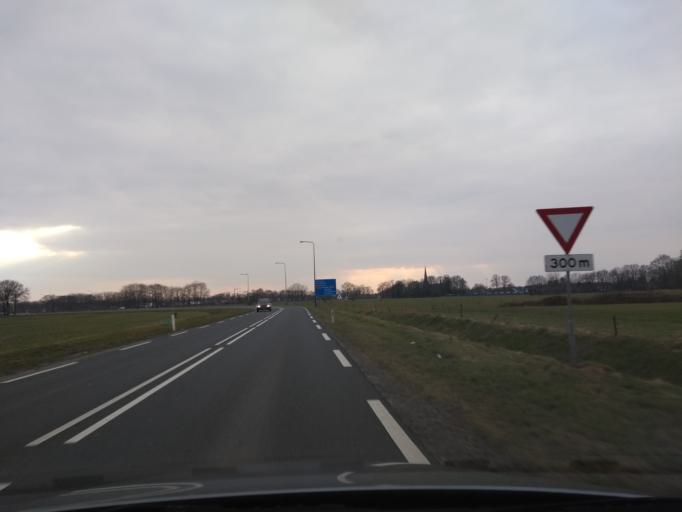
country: NL
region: Overijssel
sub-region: Gemeente Almelo
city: Almelo
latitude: 52.3785
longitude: 6.7158
